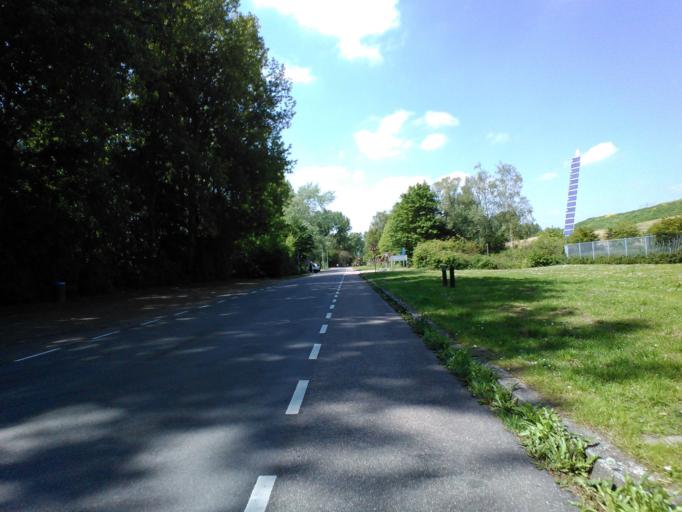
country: NL
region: South Holland
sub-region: Gemeente Sliedrecht
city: Sliedrecht
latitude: 51.8103
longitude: 4.7531
